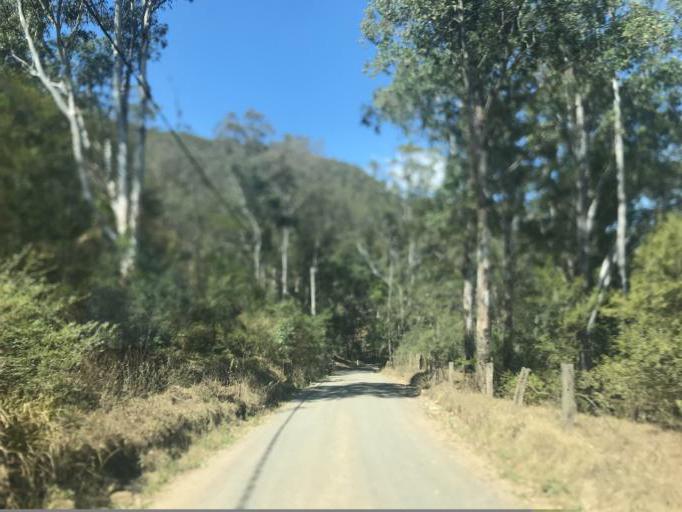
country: AU
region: New South Wales
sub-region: Hornsby Shire
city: Glenorie
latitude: -33.2786
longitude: 150.9680
